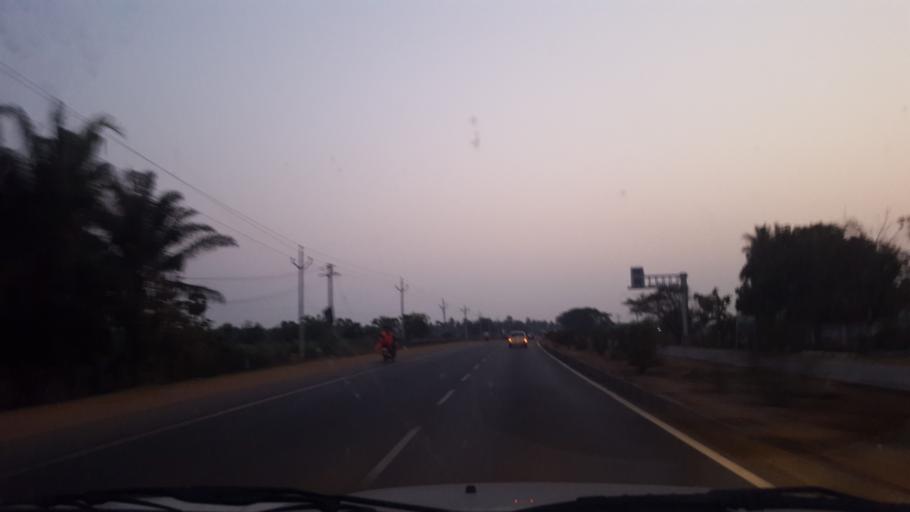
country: IN
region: Andhra Pradesh
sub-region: East Godavari
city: Peddapuram
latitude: 17.1534
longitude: 81.9878
